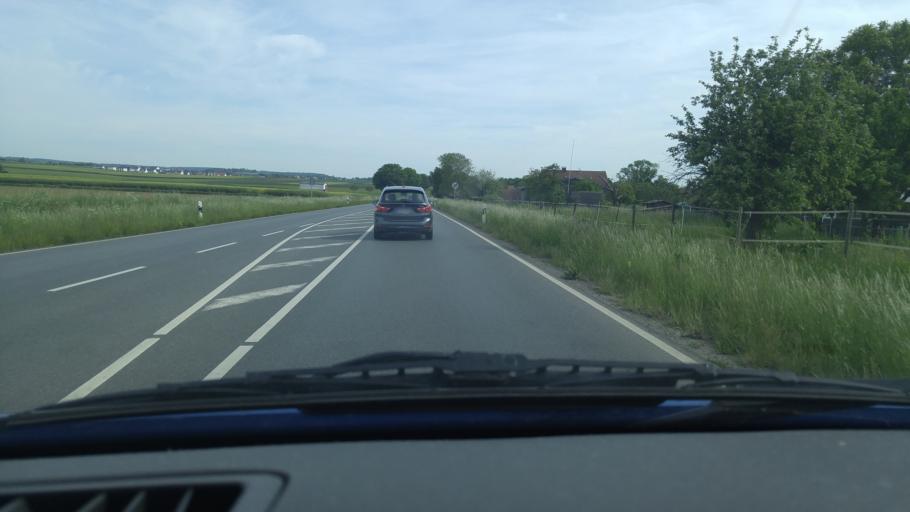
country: DE
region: Hesse
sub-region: Regierungsbezirk Darmstadt
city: Wolfersheim
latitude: 50.3780
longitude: 8.8048
